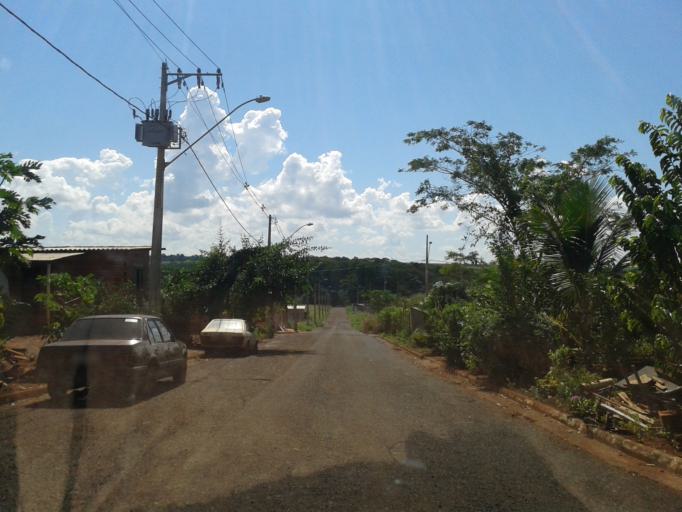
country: BR
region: Goias
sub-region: Itumbiara
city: Itumbiara
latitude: -18.4242
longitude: -49.1823
